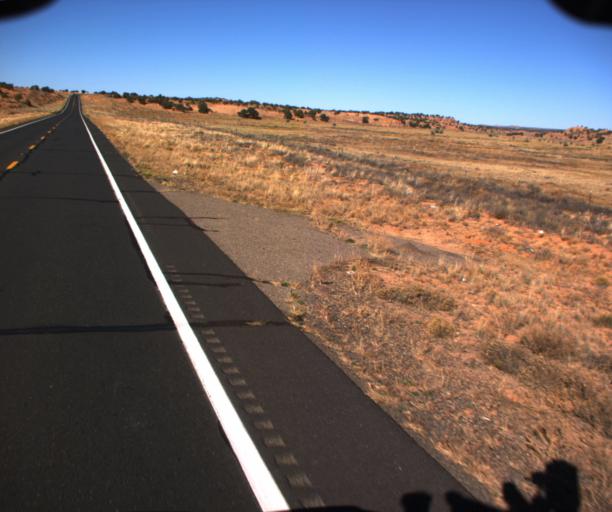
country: US
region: Arizona
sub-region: Coconino County
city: Kaibito
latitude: 36.4973
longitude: -110.7056
